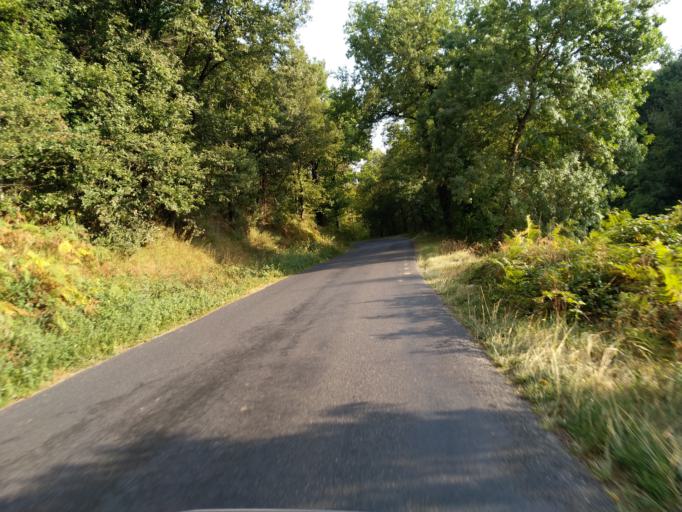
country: FR
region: Midi-Pyrenees
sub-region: Departement du Tarn
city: Frejairolles
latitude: 43.8581
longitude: 2.2343
